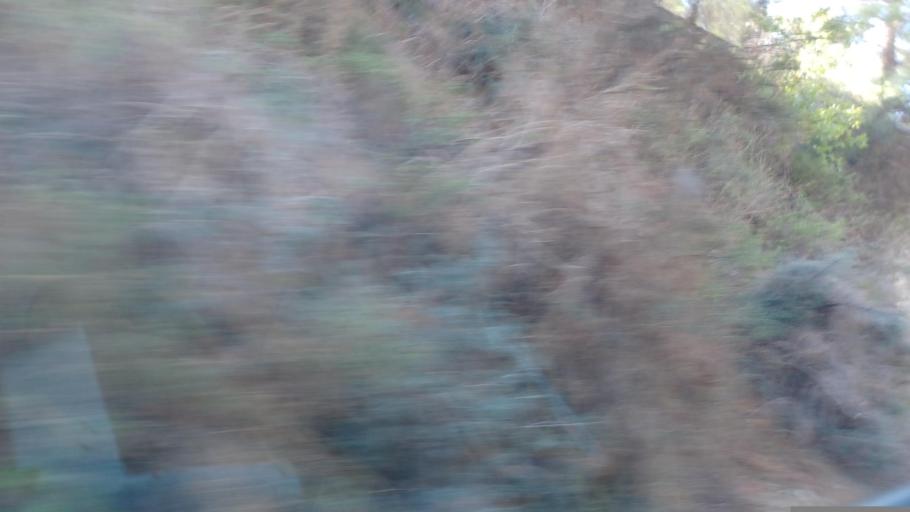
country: CY
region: Pafos
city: Polis
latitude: 35.0374
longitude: 32.5073
